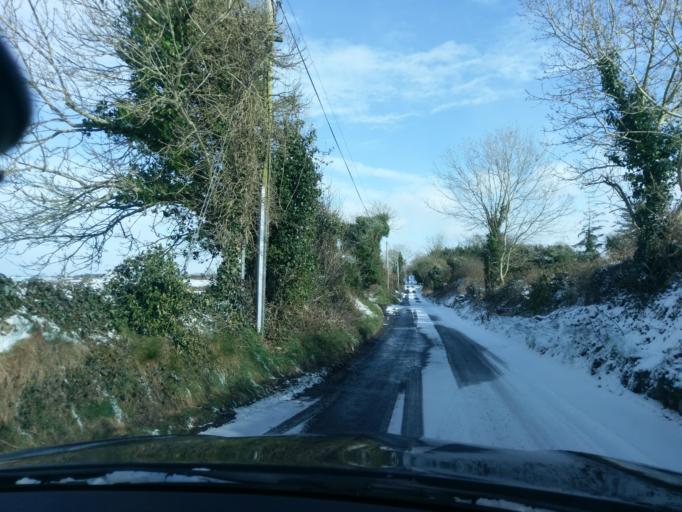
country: IE
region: Connaught
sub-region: County Galway
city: Athenry
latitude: 53.2032
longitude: -8.7594
